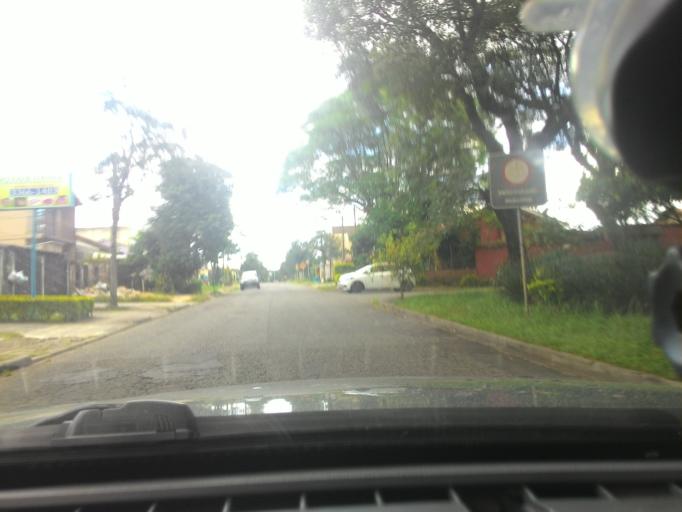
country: BR
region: Parana
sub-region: Pinhais
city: Pinhais
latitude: -25.4575
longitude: -49.2298
